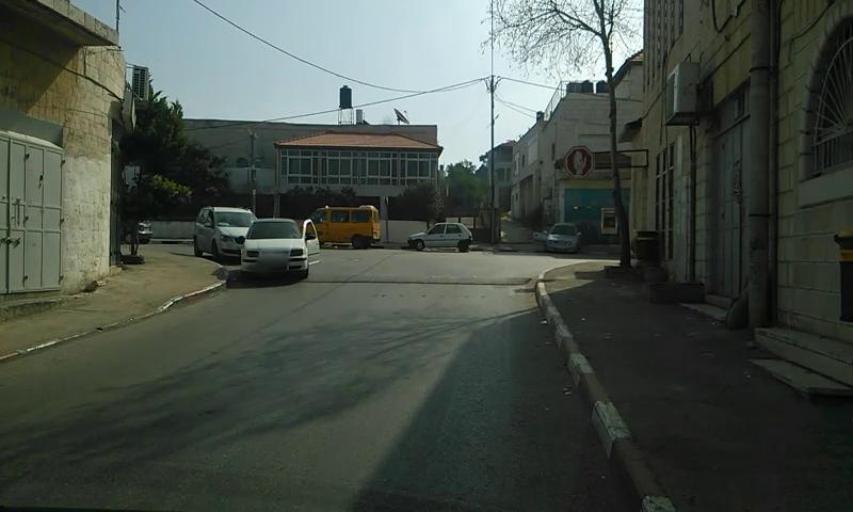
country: PS
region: West Bank
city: `Ayn Yabrud
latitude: 31.9537
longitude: 35.2517
